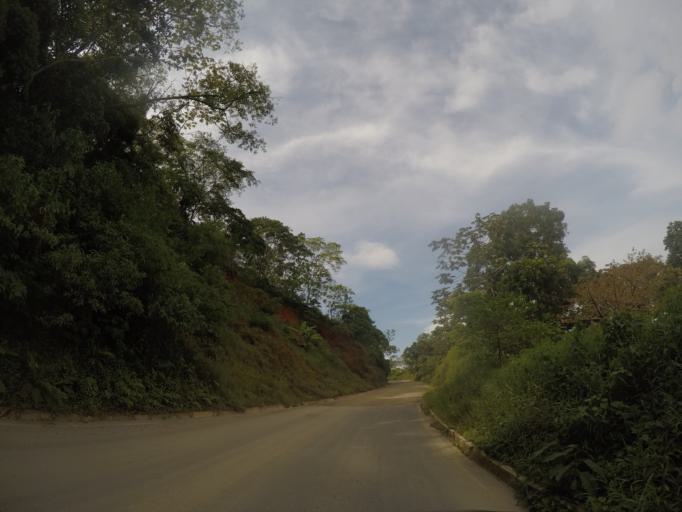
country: MX
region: Oaxaca
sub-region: San Pedro Pochutla
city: Los Naranjos Esquipulas
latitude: 15.9531
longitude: -96.4501
